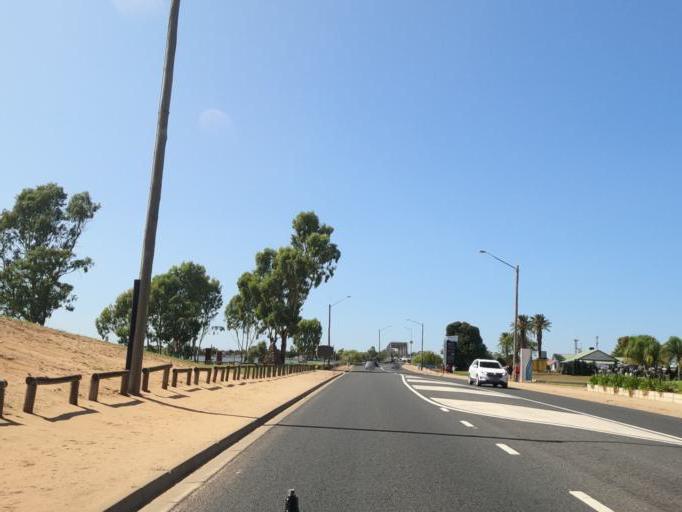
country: AU
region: New South Wales
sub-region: Corowa Shire
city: Mulwala
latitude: -36.0019
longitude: 146.0023
